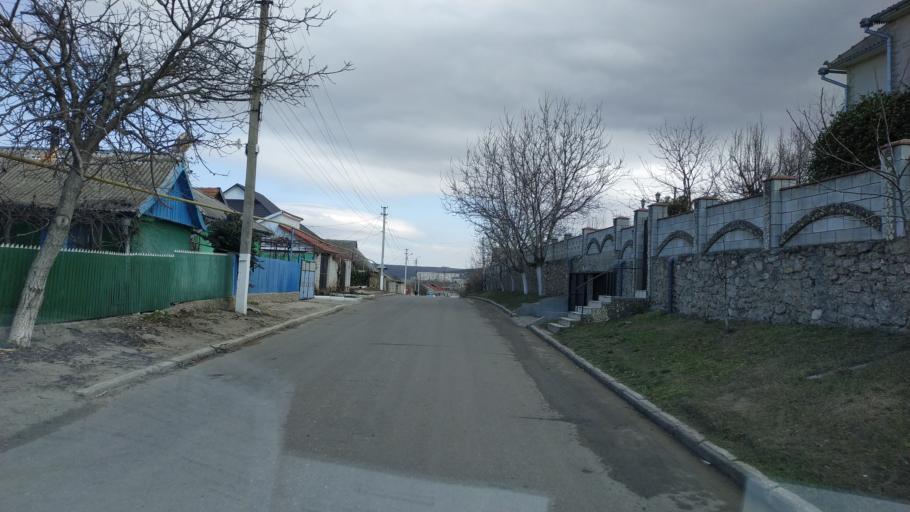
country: MD
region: Causeni
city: Causeni
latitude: 46.6443
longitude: 29.3887
